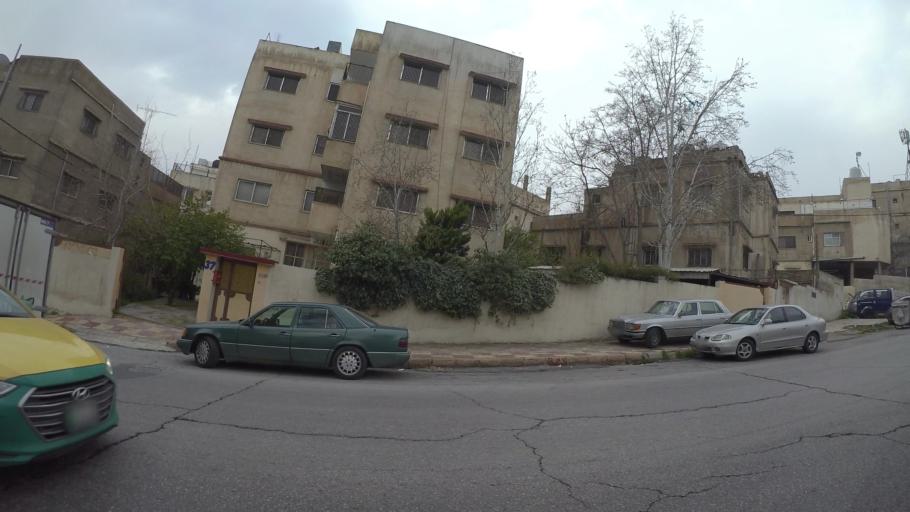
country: JO
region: Amman
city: Amman
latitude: 31.9577
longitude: 35.9443
